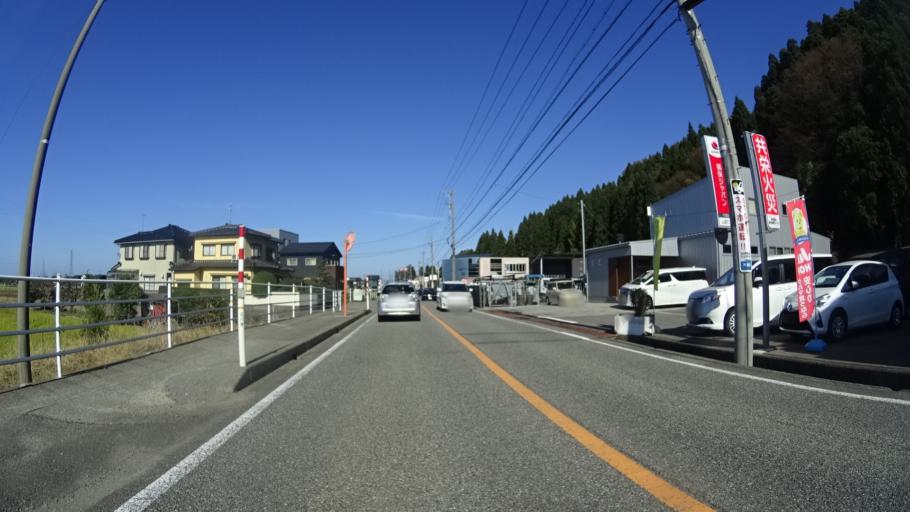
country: JP
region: Ishikawa
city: Tsurugi-asahimachi
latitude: 36.4691
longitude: 136.6178
